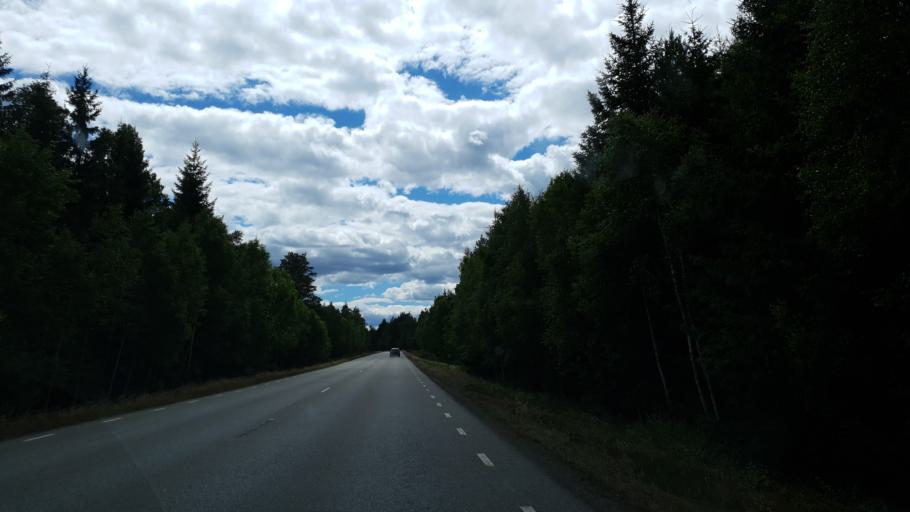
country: SE
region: Kalmar
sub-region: Emmaboda Kommun
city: Emmaboda
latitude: 56.9294
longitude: 15.5759
